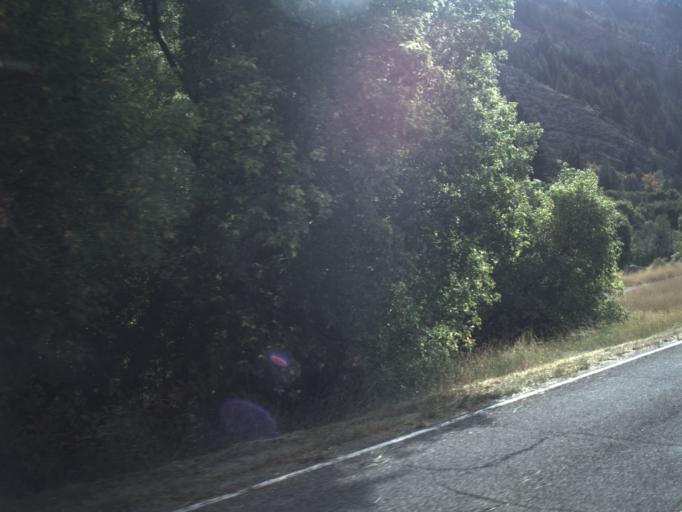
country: US
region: Utah
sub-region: Cache County
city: Millville
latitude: 41.6276
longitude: -111.6811
